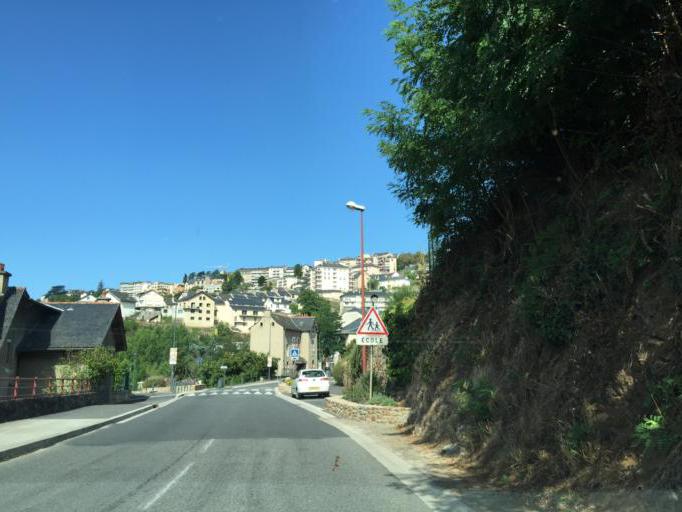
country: FR
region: Midi-Pyrenees
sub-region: Departement de l'Aveyron
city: Le Monastere
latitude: 44.3438
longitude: 2.5820
